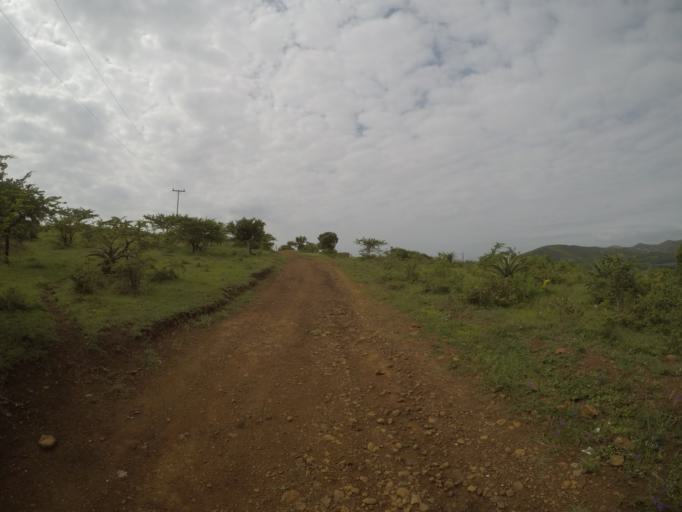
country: ZA
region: KwaZulu-Natal
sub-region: uThungulu District Municipality
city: Empangeni
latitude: -28.6243
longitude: 31.9005
